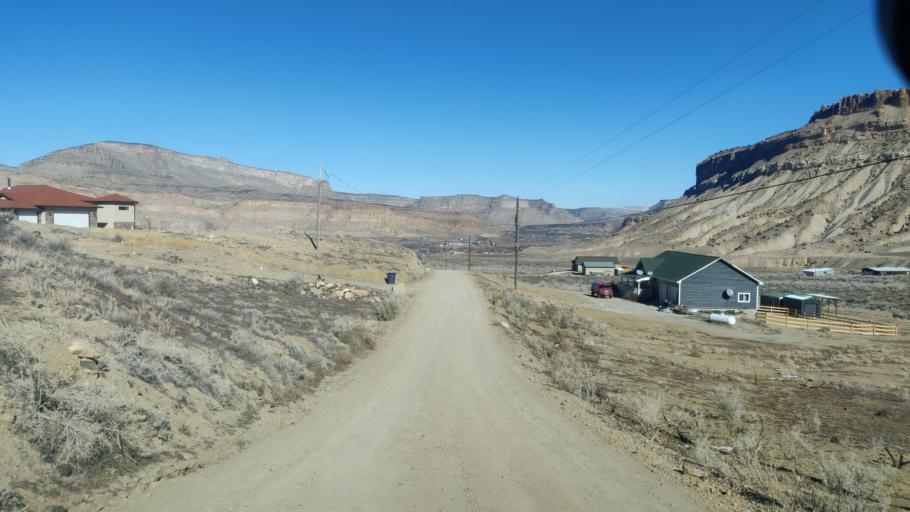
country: US
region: Colorado
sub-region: Mesa County
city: Palisade
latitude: 39.0882
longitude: -108.3297
